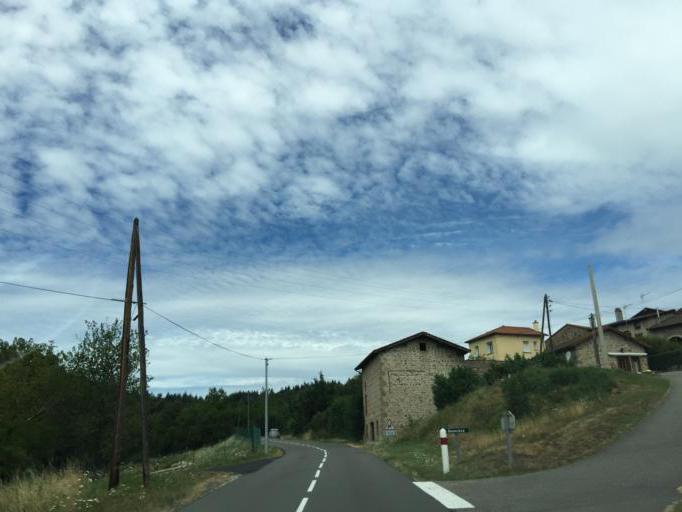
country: FR
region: Rhone-Alpes
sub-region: Departement de la Loire
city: Saint-Bonnet-le-Chateau
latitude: 45.4084
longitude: 4.1066
